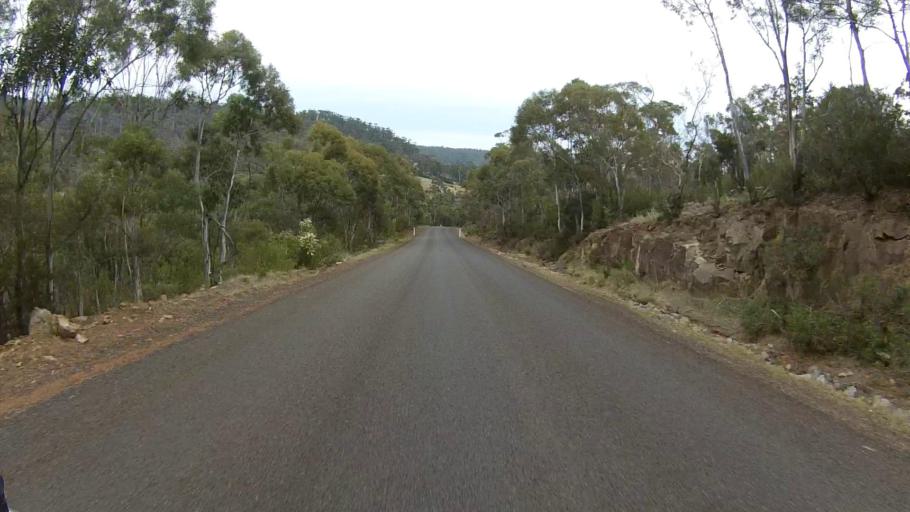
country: AU
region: Tasmania
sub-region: Sorell
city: Sorell
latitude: -42.5747
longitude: 147.8744
